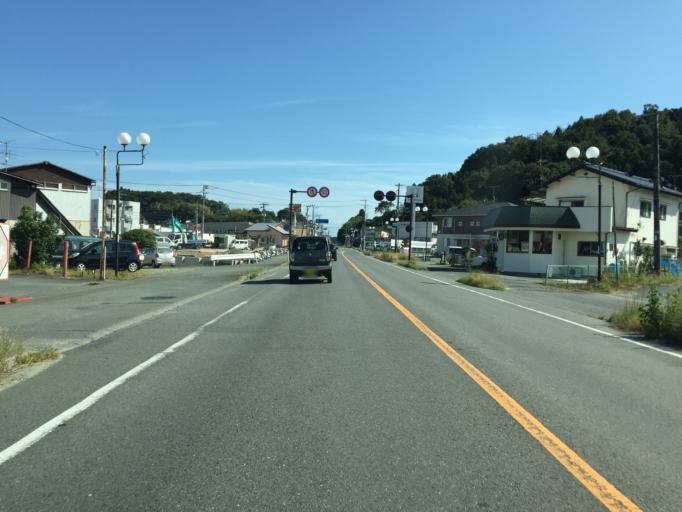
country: JP
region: Fukushima
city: Iwaki
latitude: 37.0586
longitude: 140.8698
